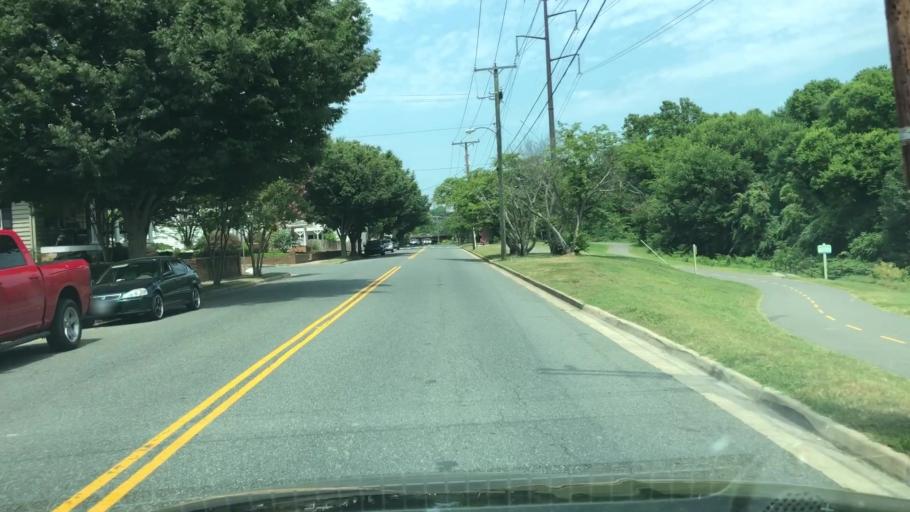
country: US
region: Virginia
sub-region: Stafford County
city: Falmouth
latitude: 38.3167
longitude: -77.4691
